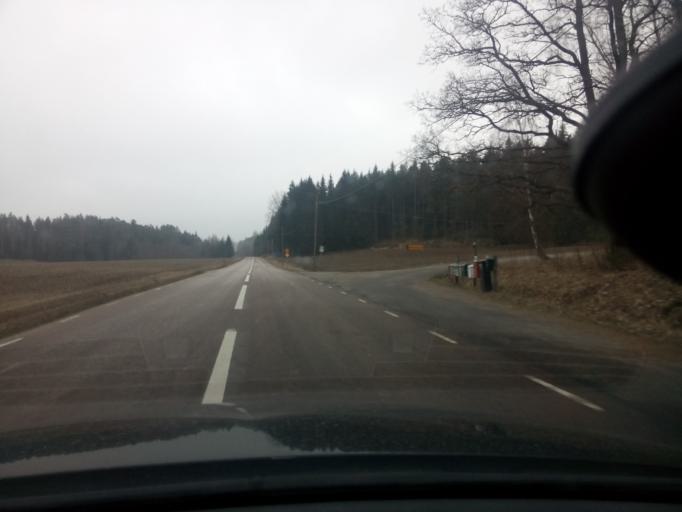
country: SE
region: Soedermanland
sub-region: Gnesta Kommun
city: Gnesta
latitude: 59.0105
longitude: 17.1724
